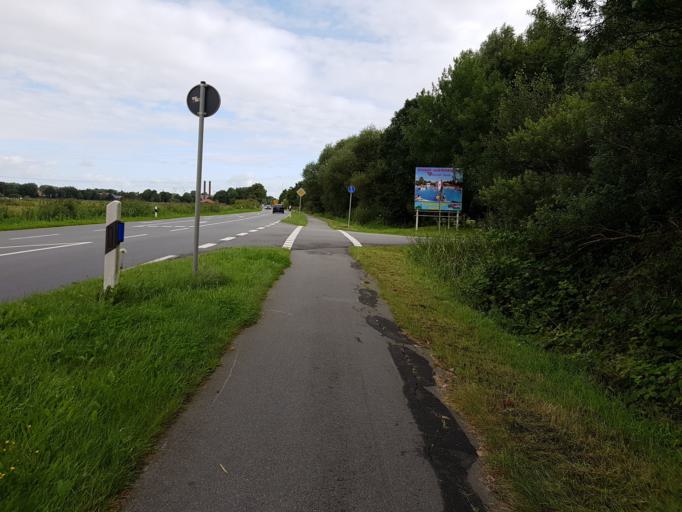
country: DE
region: Lower Saxony
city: Wittmund
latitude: 53.5623
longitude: 7.7842
